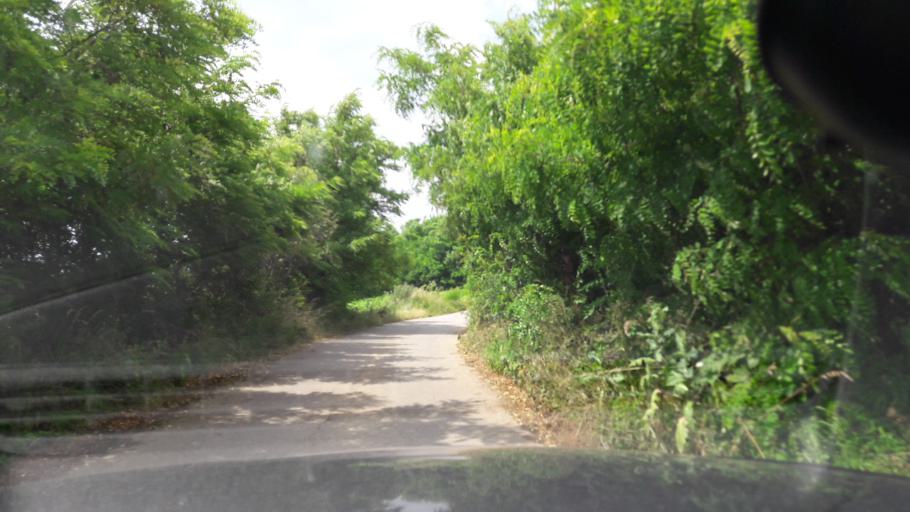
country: RS
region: Central Serbia
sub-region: Belgrade
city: Sopot
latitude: 44.6149
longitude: 20.5987
